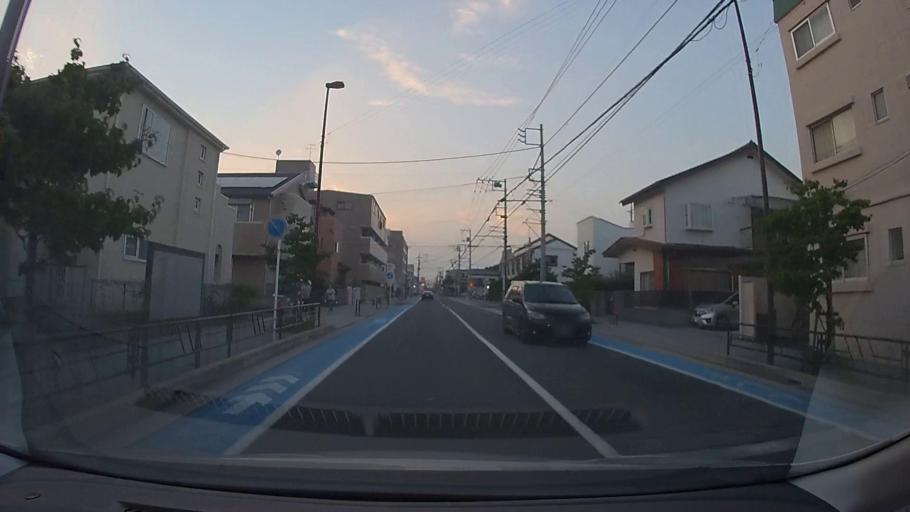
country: JP
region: Kanagawa
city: Minami-rinkan
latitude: 35.4923
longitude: 139.4460
